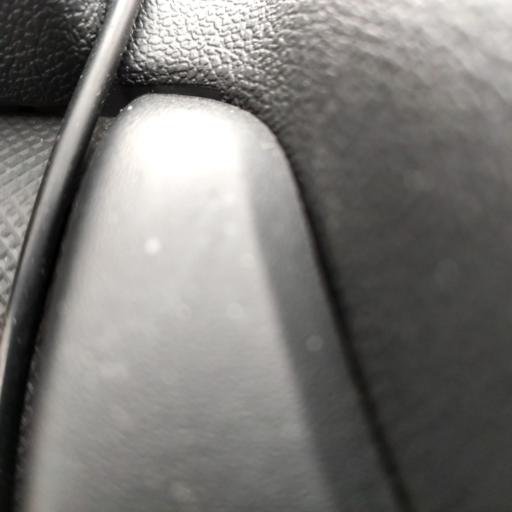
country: RU
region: Voronezj
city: Ostrogozhsk
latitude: 50.8435
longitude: 39.0336
